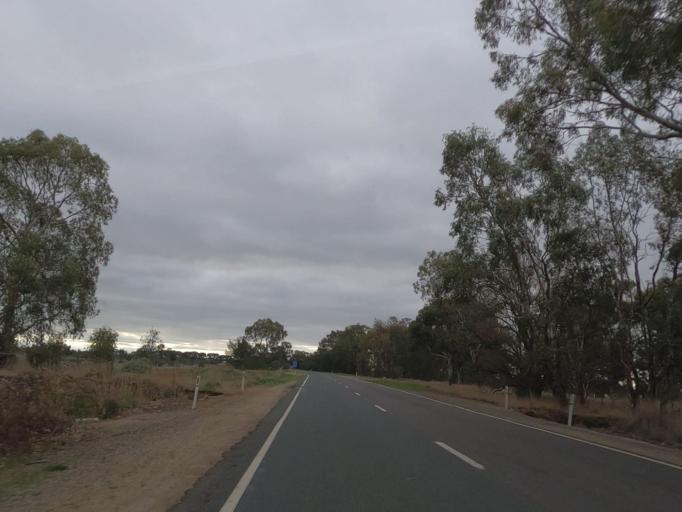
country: AU
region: Victoria
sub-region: Swan Hill
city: Swan Hill
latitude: -35.9478
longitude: 143.9405
